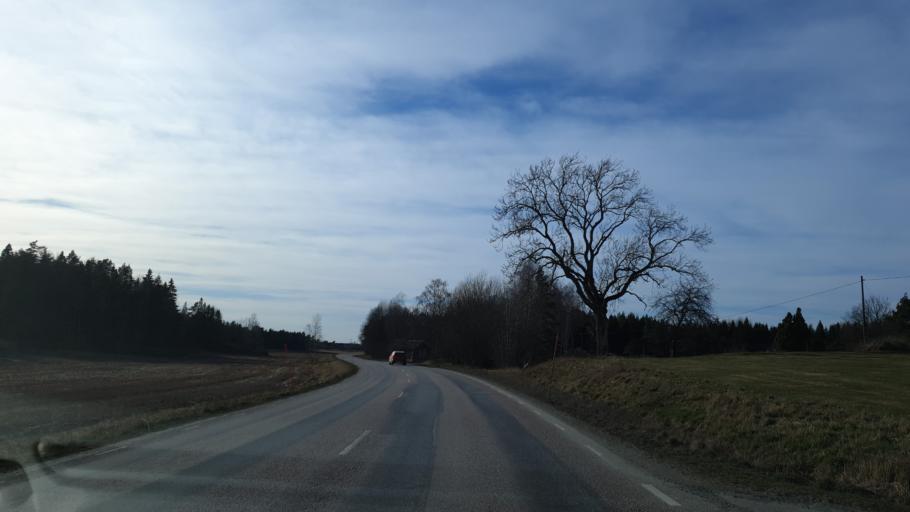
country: SE
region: Uppsala
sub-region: Enkopings Kommun
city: Grillby
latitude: 59.5964
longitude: 17.1726
